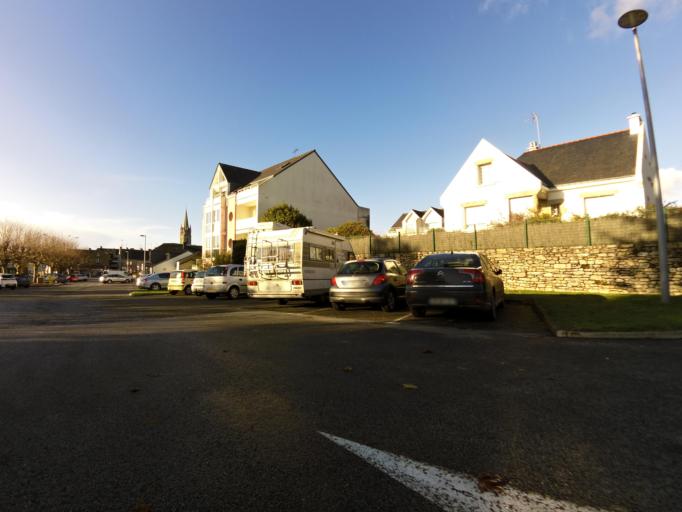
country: FR
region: Brittany
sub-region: Departement du Morbihan
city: Questembert
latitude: 47.6603
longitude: -2.4511
